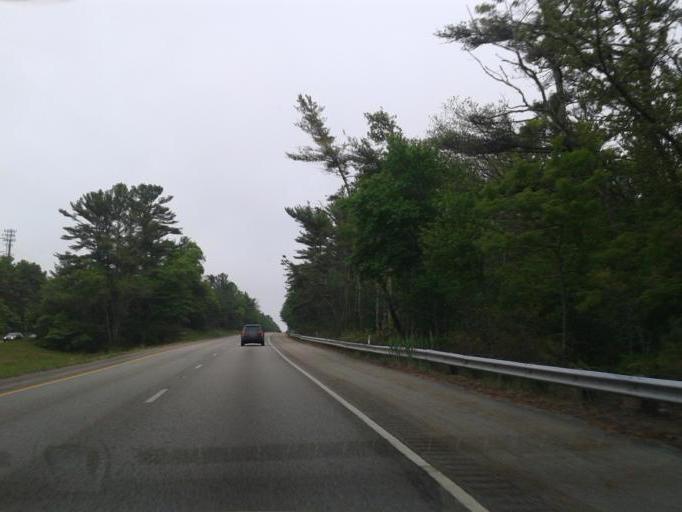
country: US
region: Massachusetts
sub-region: Plymouth County
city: White Island Shores
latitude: 41.8530
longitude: -70.5795
